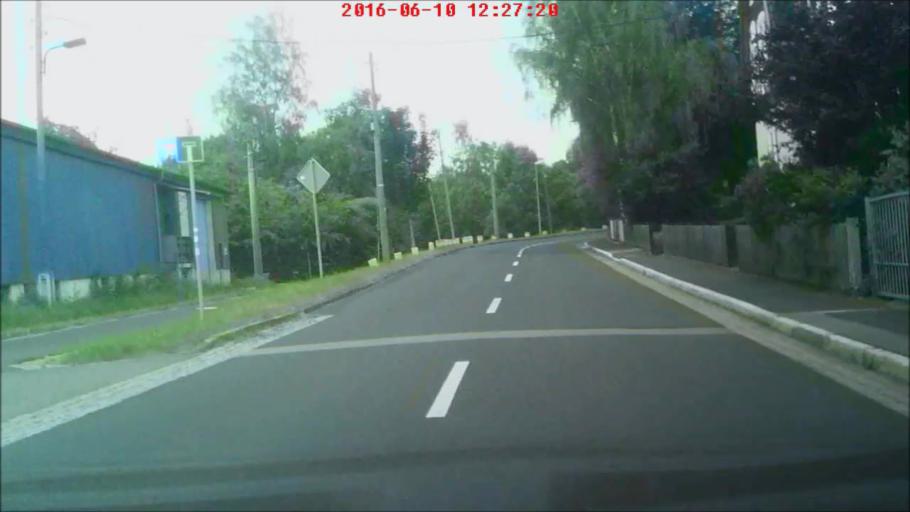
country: DE
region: Thuringia
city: Untermassfeld
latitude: 50.5348
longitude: 10.4128
